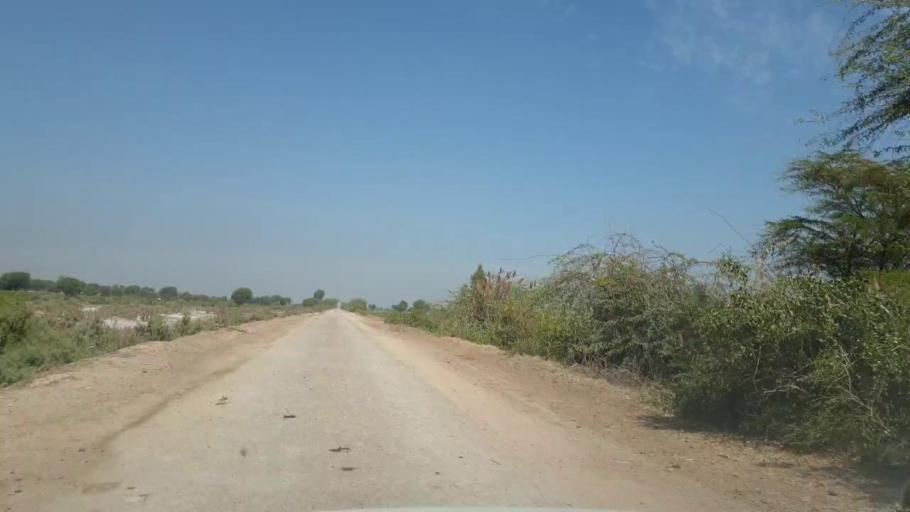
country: PK
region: Sindh
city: Pithoro
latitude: 25.5803
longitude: 69.2010
